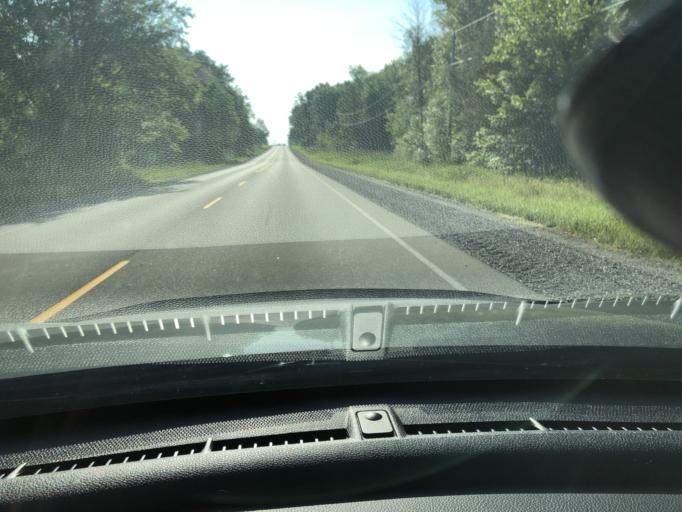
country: CA
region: Ontario
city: Stratford
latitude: 43.4246
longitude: -80.7948
